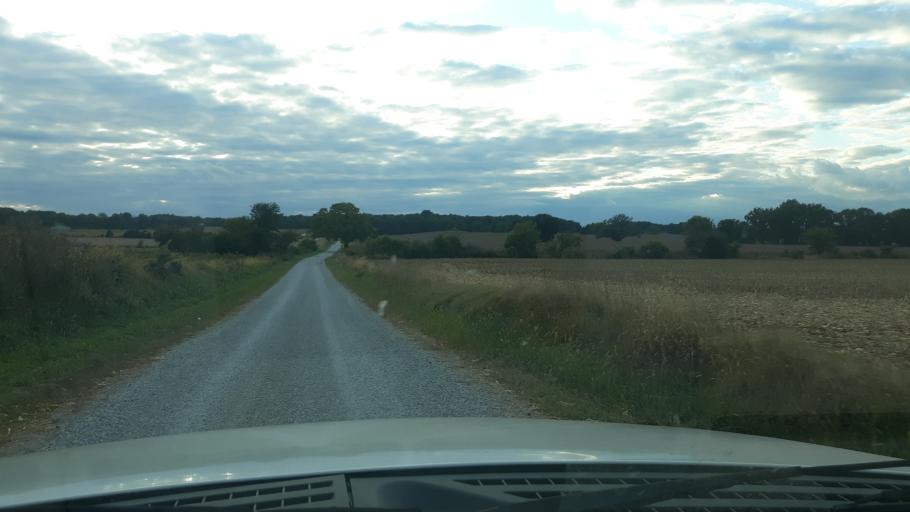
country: US
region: Illinois
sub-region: Saline County
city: Eldorado
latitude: 37.8372
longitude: -88.4701
